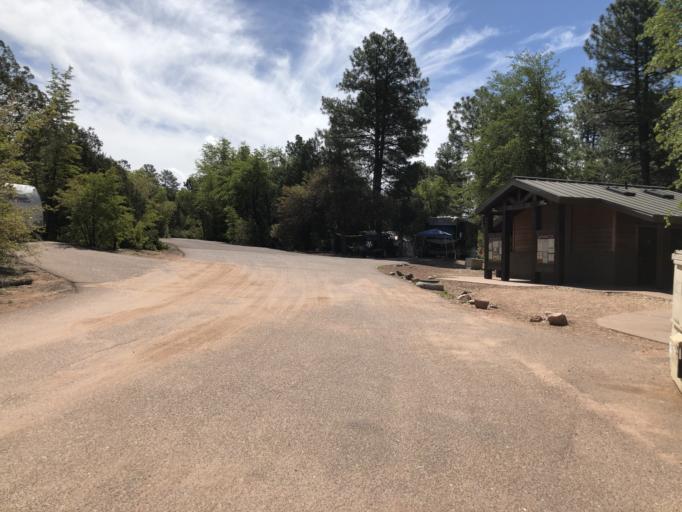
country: US
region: Arizona
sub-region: Gila County
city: Payson
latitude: 34.2723
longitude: -111.3161
